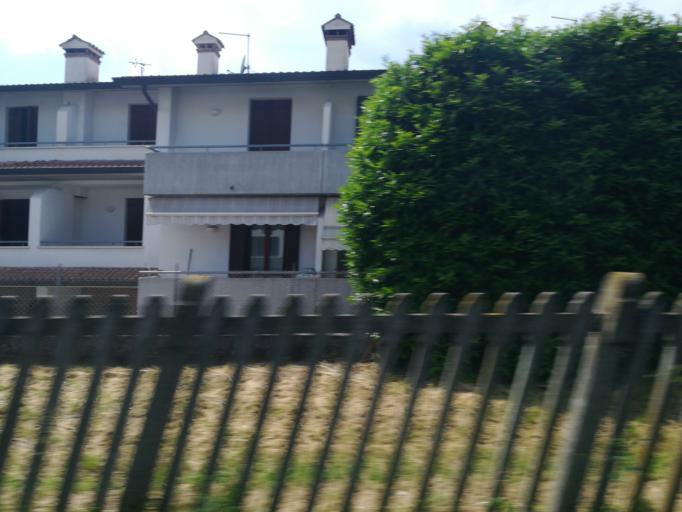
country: IT
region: Veneto
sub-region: Provincia di Vicenza
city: Monticello Conte Otto
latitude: 45.6049
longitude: 11.5703
